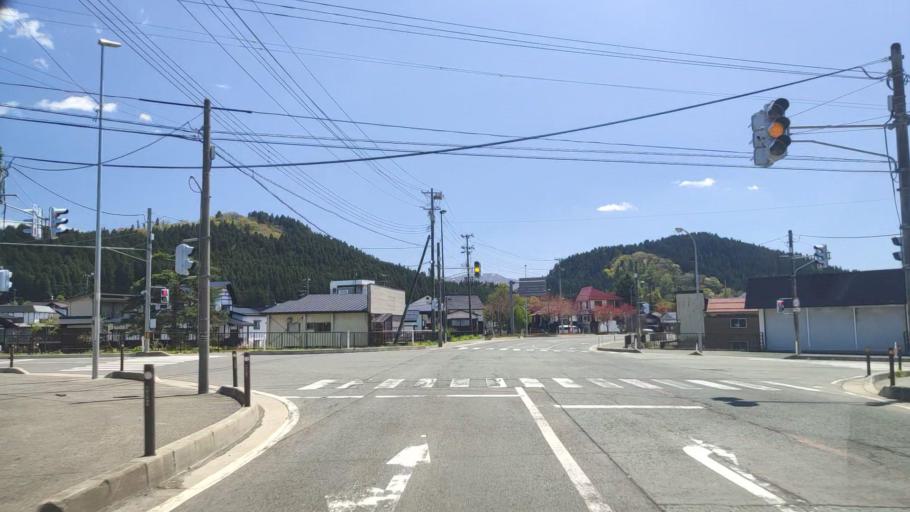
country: JP
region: Yamagata
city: Shinjo
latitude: 38.8839
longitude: 140.3362
